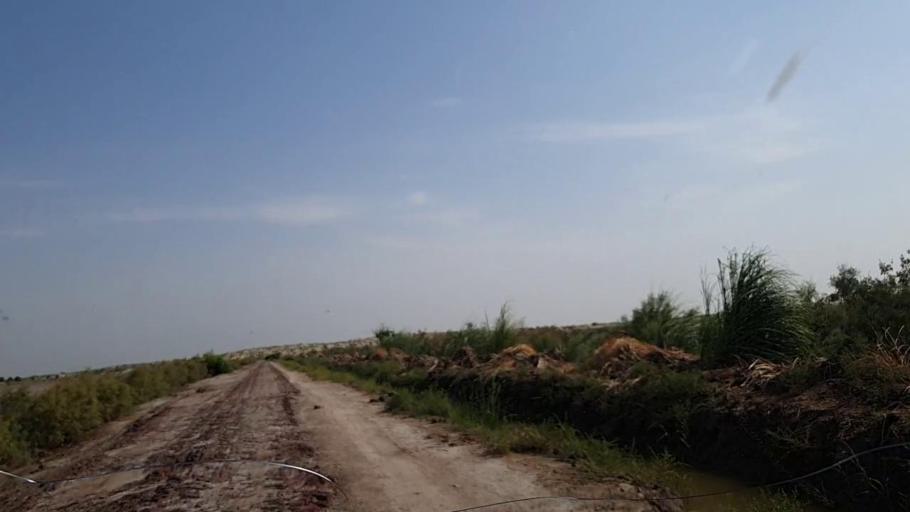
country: PK
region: Sindh
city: Khanpur
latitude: 27.6793
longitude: 69.3682
